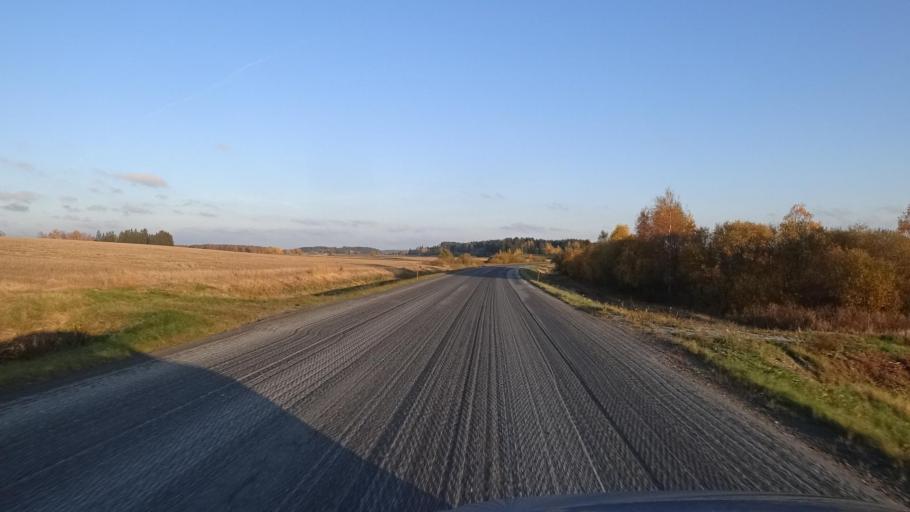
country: FI
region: Haeme
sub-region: Forssa
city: Ypaejae
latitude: 60.7862
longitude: 23.2981
